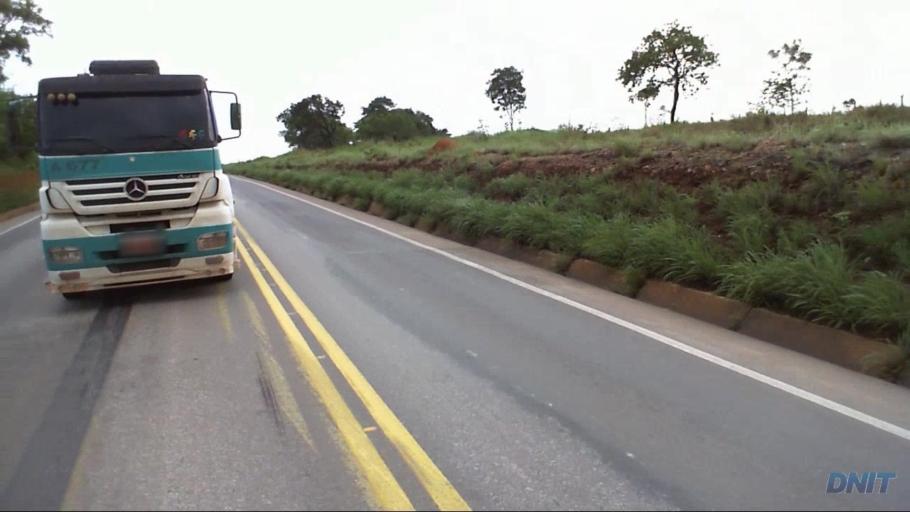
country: BR
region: Goias
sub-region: Uruacu
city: Uruacu
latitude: -14.6105
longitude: -49.1681
